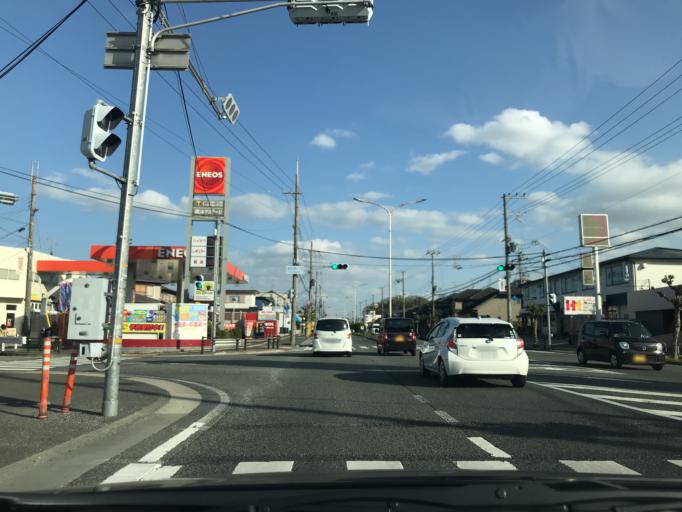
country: JP
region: Hyogo
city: Kawanishi
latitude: 34.8716
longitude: 135.3885
